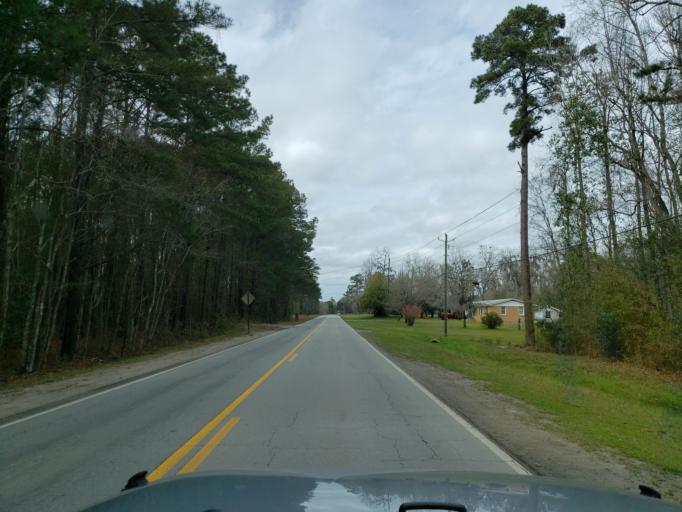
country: US
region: Georgia
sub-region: Chatham County
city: Georgetown
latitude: 32.0381
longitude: -81.2748
